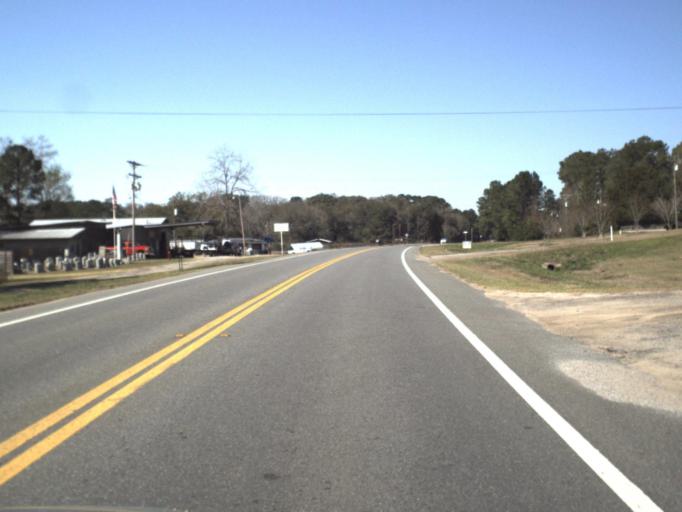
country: US
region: Florida
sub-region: Jackson County
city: Sneads
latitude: 30.7098
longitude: -84.9374
